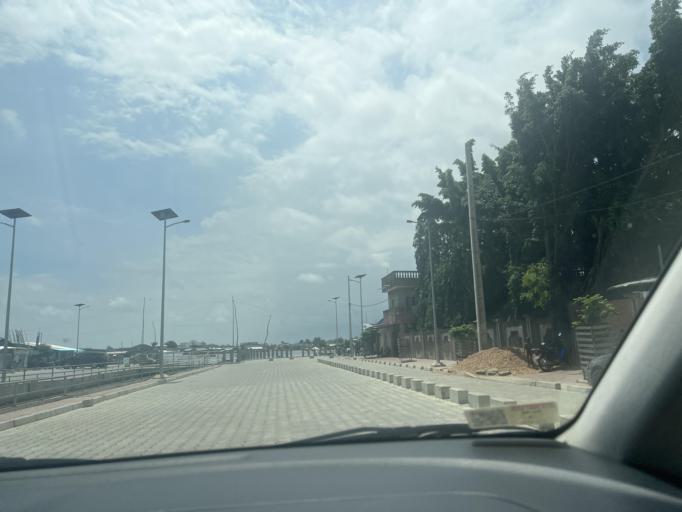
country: BJ
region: Littoral
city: Cotonou
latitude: 6.3887
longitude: 2.4382
